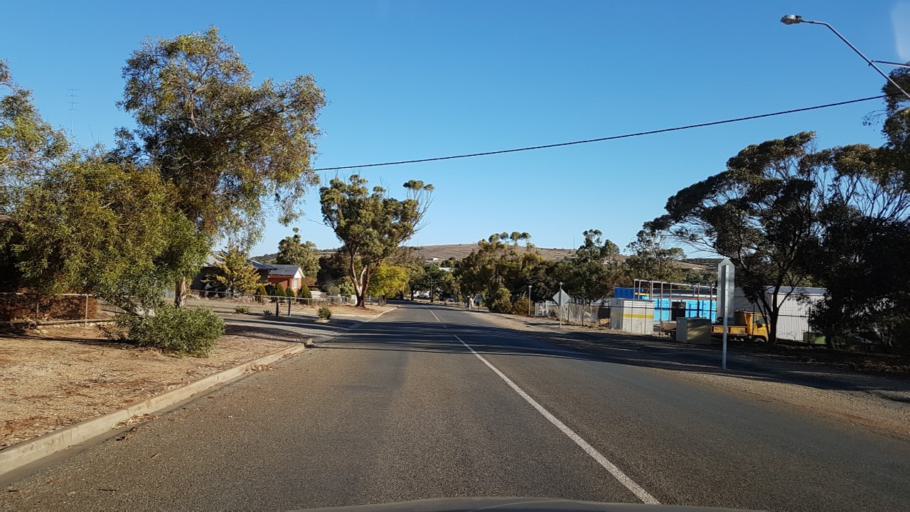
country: AU
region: South Australia
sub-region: Clare and Gilbert Valleys
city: Clare
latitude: -33.6781
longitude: 138.9409
